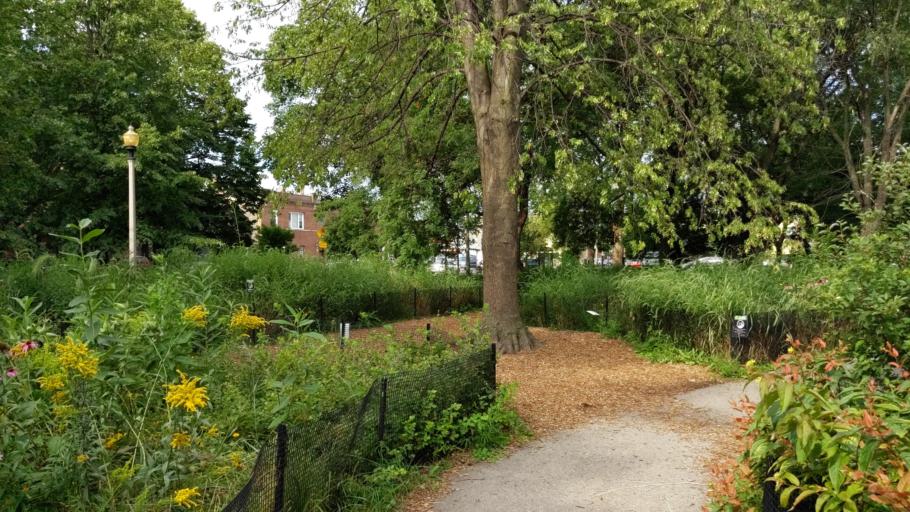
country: US
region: Illinois
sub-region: Cook County
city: Lincolnwood
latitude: 41.9617
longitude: -87.6876
